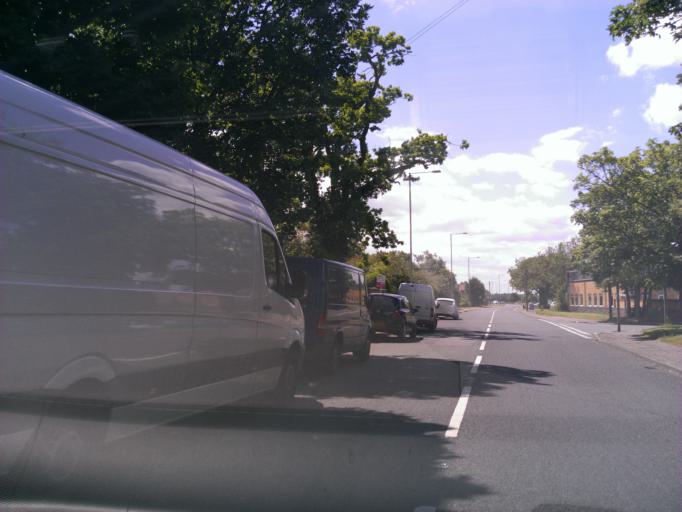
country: GB
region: England
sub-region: Essex
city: Layer de la Haye
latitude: 51.8722
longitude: 0.8605
